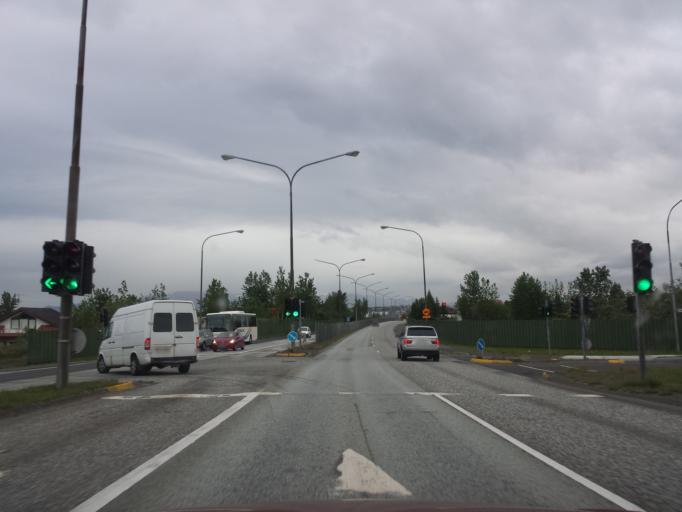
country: IS
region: Capital Region
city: Gardabaer
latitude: 64.0883
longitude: -21.9345
